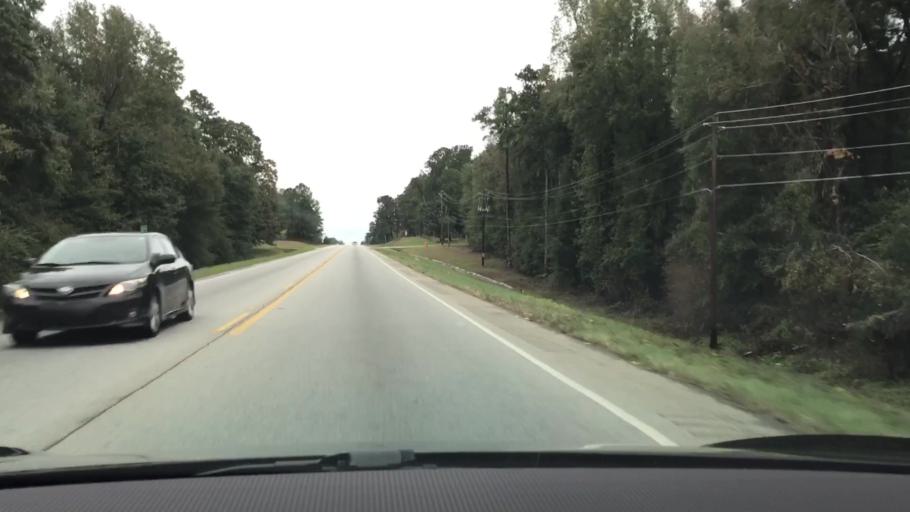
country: US
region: Georgia
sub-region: Jefferson County
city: Louisville
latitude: 33.0012
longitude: -82.3953
